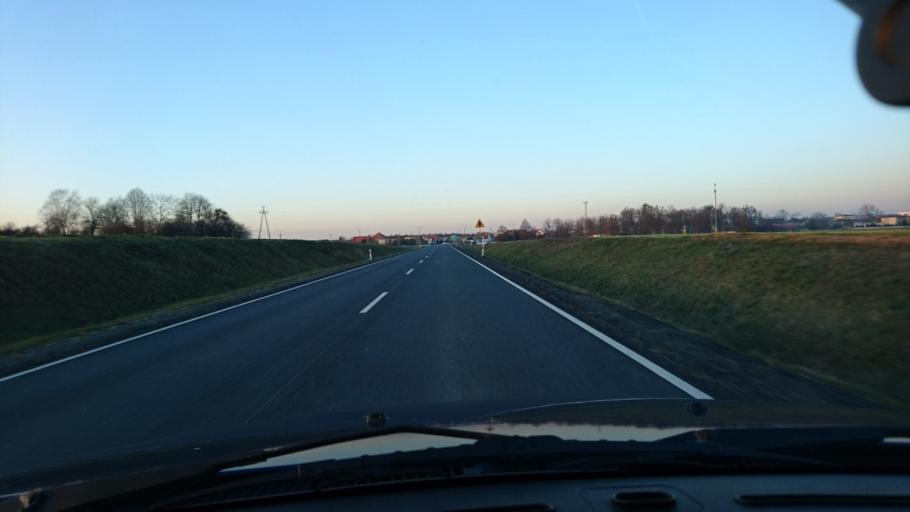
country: PL
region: Silesian Voivodeship
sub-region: Powiat gliwicki
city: Wielowies
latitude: 50.5008
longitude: 18.6055
